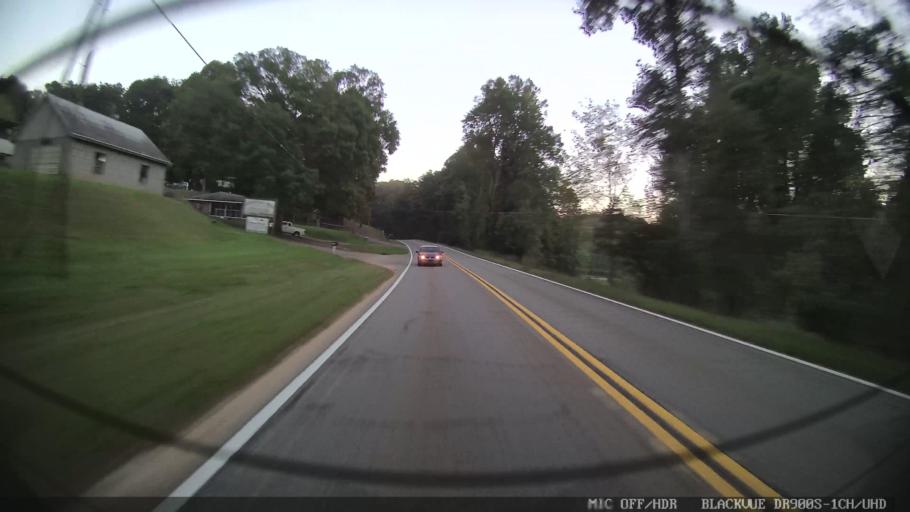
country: US
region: Georgia
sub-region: Gilmer County
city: Ellijay
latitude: 34.7168
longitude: -84.5025
